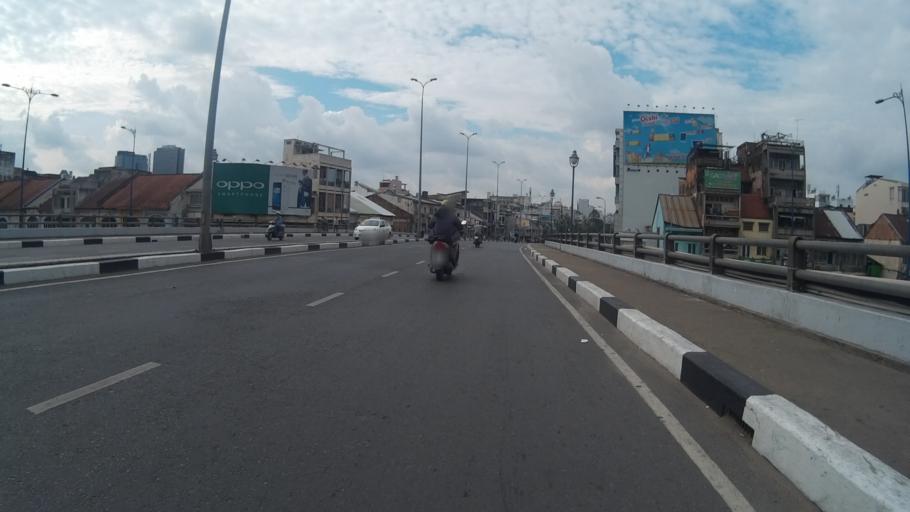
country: VN
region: Ho Chi Minh City
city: Quan Bon
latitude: 10.7637
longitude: 106.6982
